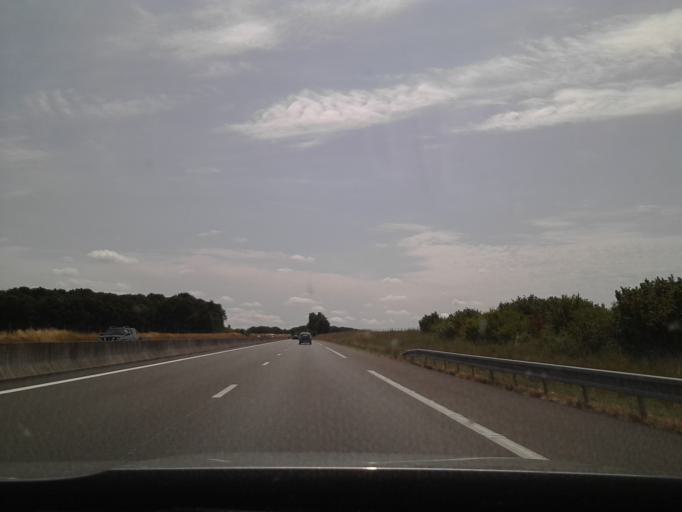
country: FR
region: Centre
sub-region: Departement d'Indre-et-Loire
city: Neuille-Pont-Pierre
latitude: 47.5917
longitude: 0.5498
